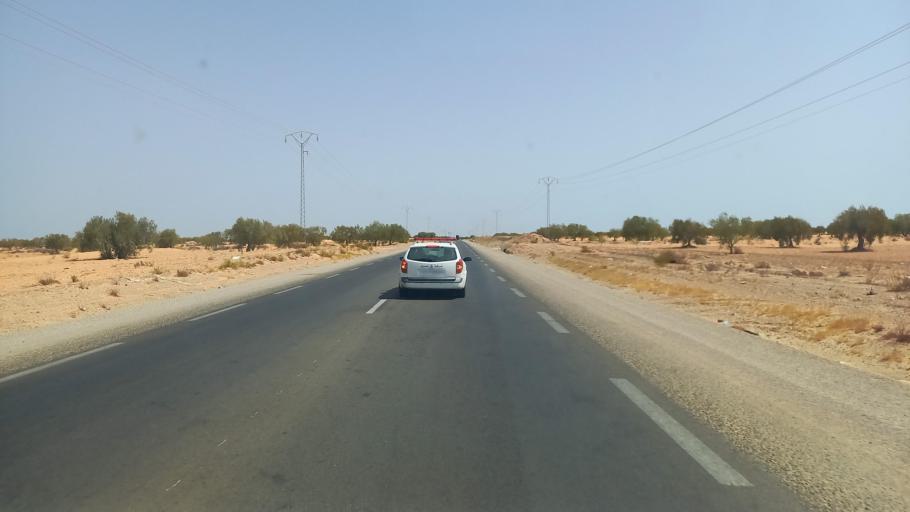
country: TN
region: Madanin
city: Zarzis
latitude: 33.4194
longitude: 10.8767
